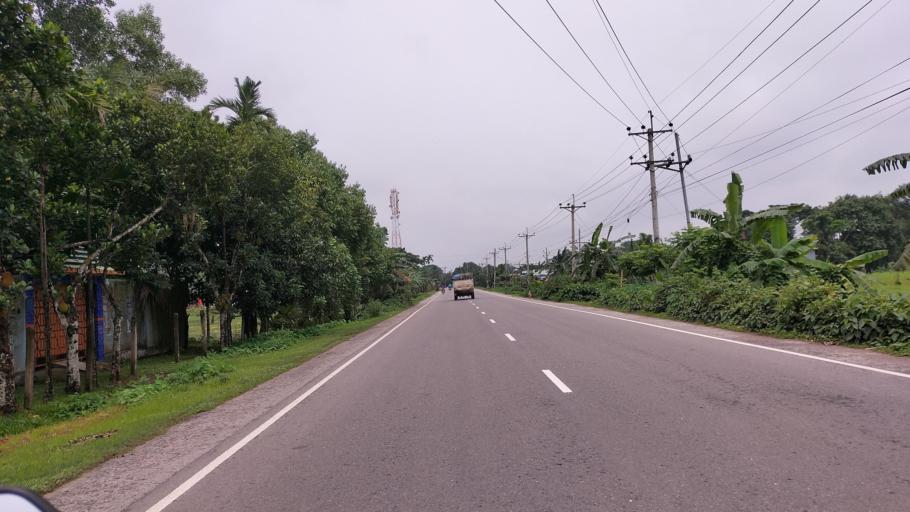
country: BD
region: Dhaka
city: Netrakona
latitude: 24.8497
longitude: 90.6408
